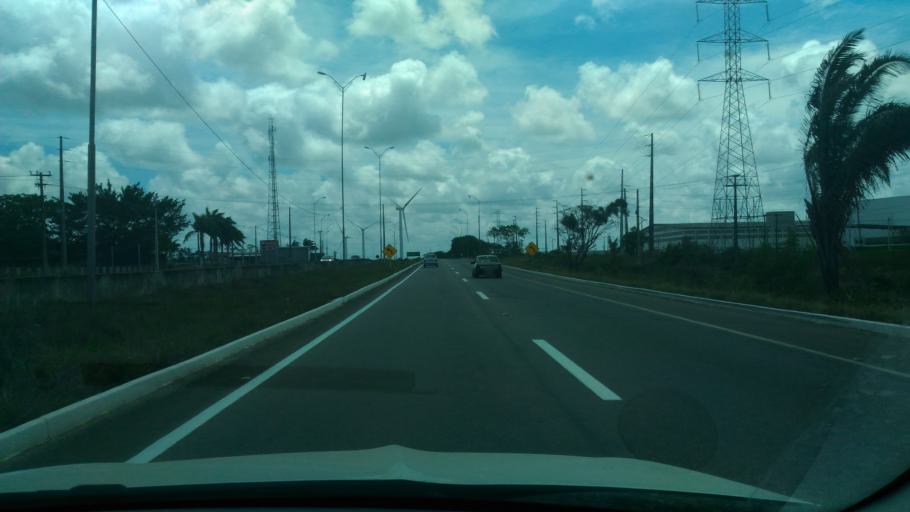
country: BR
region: Paraiba
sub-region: Conde
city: Conde
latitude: -7.2545
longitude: -34.9342
